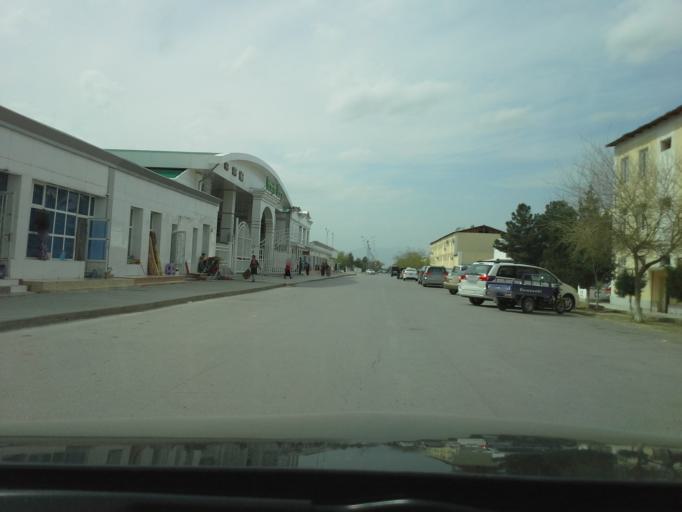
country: TM
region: Ahal
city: Abadan
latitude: 38.0577
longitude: 58.1524
